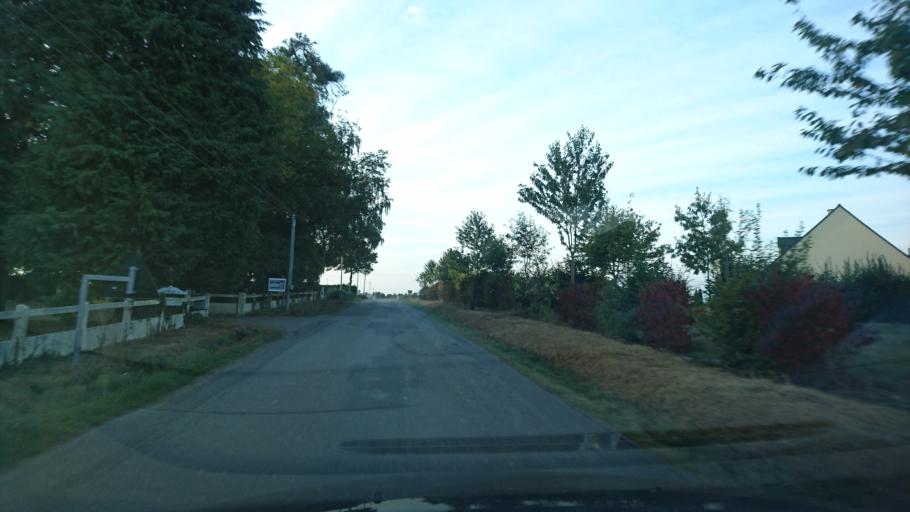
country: FR
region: Brittany
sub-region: Departement d'Ille-et-Vilaine
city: Sixt-sur-Aff
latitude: 47.7620
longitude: -2.0655
